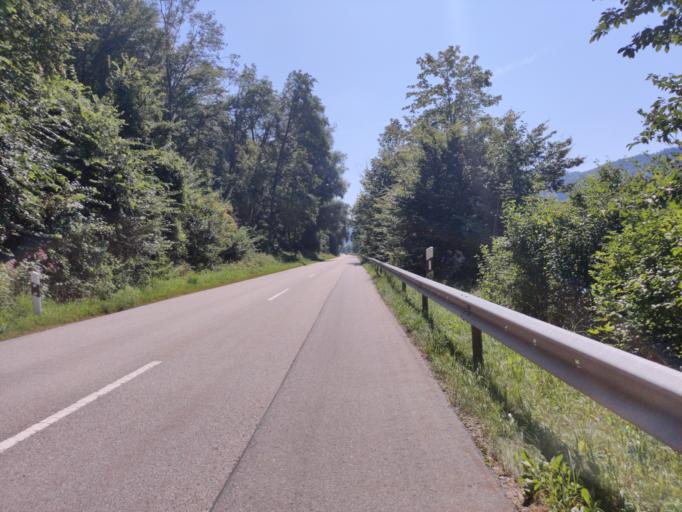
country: DE
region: Bavaria
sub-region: Lower Bavaria
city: Untergriesbach
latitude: 48.5245
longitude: 13.6980
